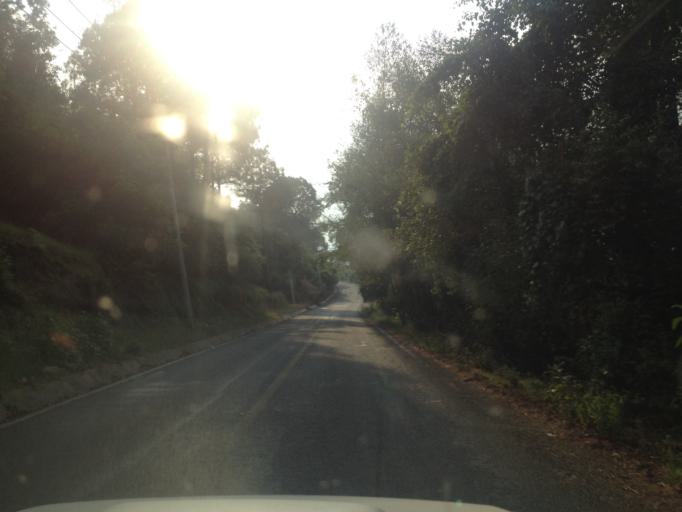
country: MX
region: Michoacan
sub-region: Zitacuaro
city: Macutzio
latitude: 19.4885
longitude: -100.3219
